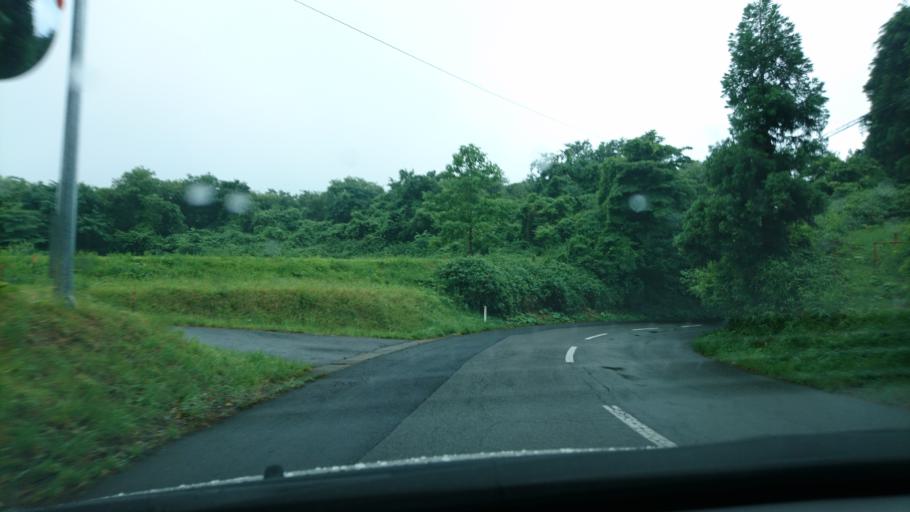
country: JP
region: Iwate
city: Ichinoseki
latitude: 38.9075
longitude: 141.0328
